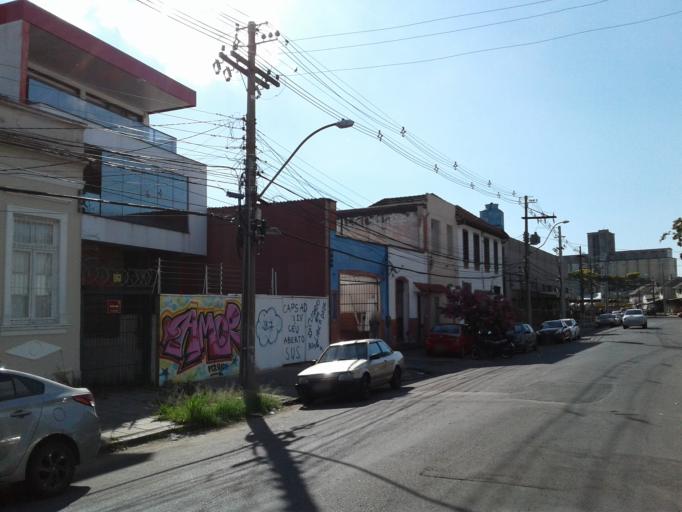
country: BR
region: Rio Grande do Sul
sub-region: Porto Alegre
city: Porto Alegre
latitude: -30.0192
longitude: -51.2129
